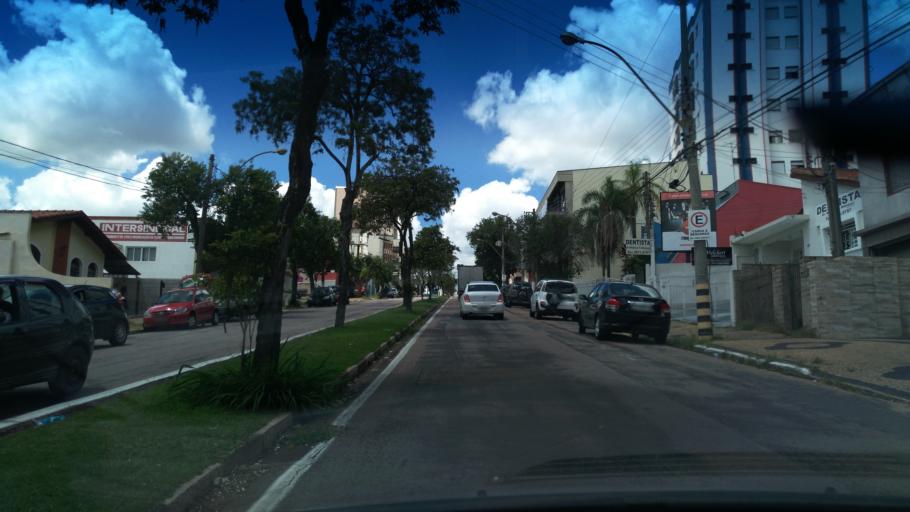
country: BR
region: Sao Paulo
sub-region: Valinhos
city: Valinhos
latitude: -22.9739
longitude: -46.9969
